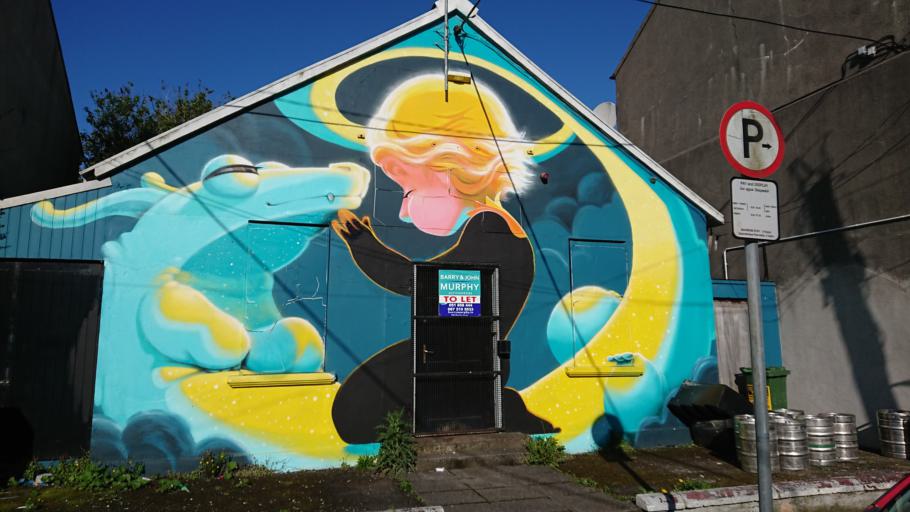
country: IE
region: Munster
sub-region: Waterford
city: Waterford
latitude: 52.2591
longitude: -7.1153
